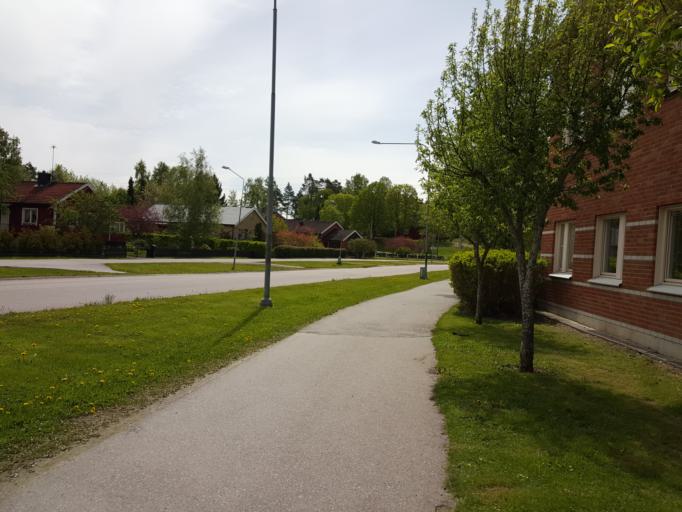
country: SE
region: Uppsala
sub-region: Osthammars Kommun
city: Gimo
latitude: 60.1716
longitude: 18.1856
